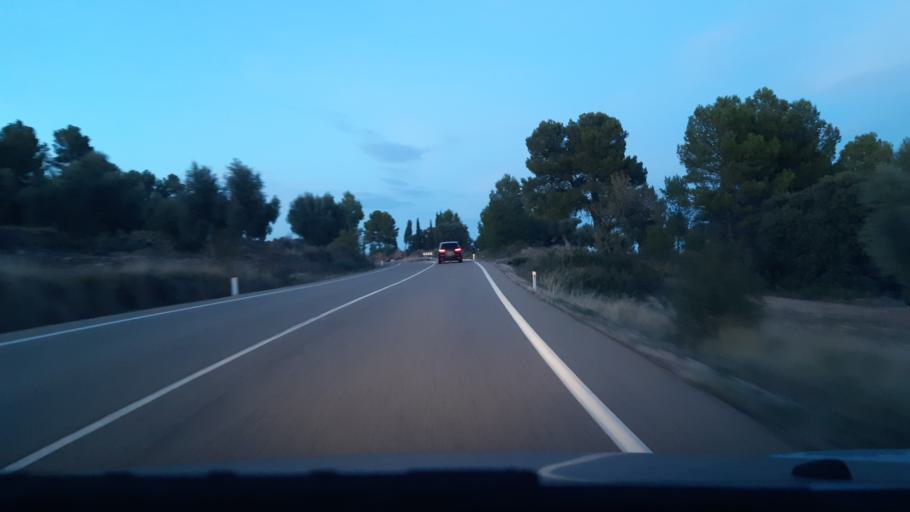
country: ES
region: Aragon
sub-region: Provincia de Teruel
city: Calaceite
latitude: 40.9804
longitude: 0.2015
